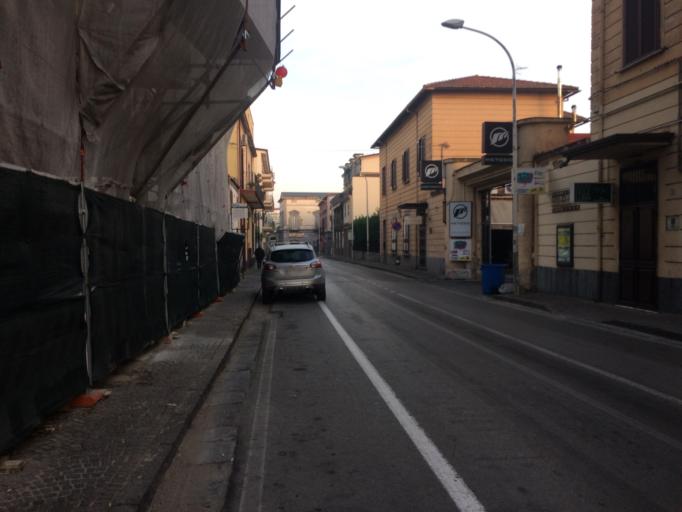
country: IT
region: Campania
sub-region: Provincia di Napoli
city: Frattamaggiore
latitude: 40.9387
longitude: 14.2673
